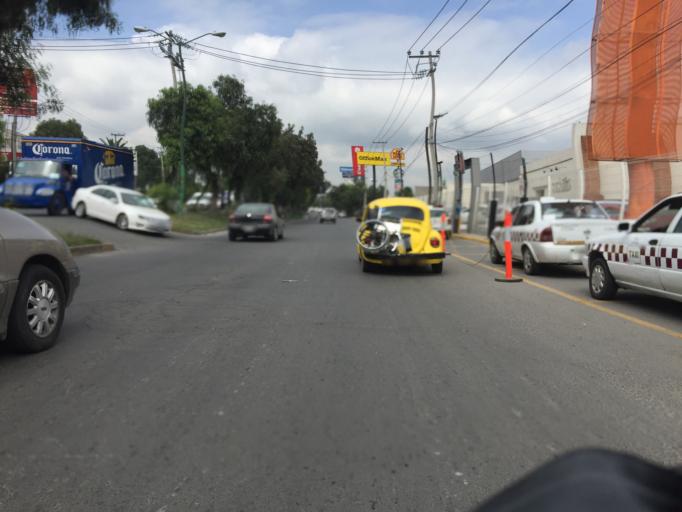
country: MX
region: Mexico
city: Cuautitlan
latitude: 19.6703
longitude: -99.2016
